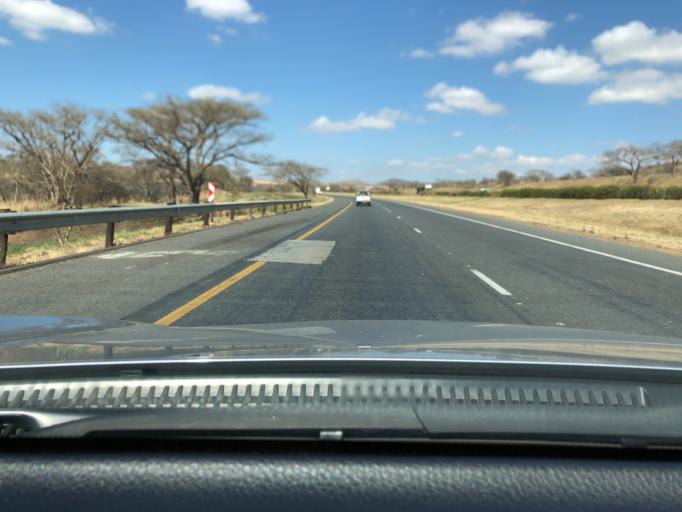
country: ZA
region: KwaZulu-Natal
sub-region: uThukela District Municipality
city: Estcourt
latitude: -28.9683
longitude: 29.7940
